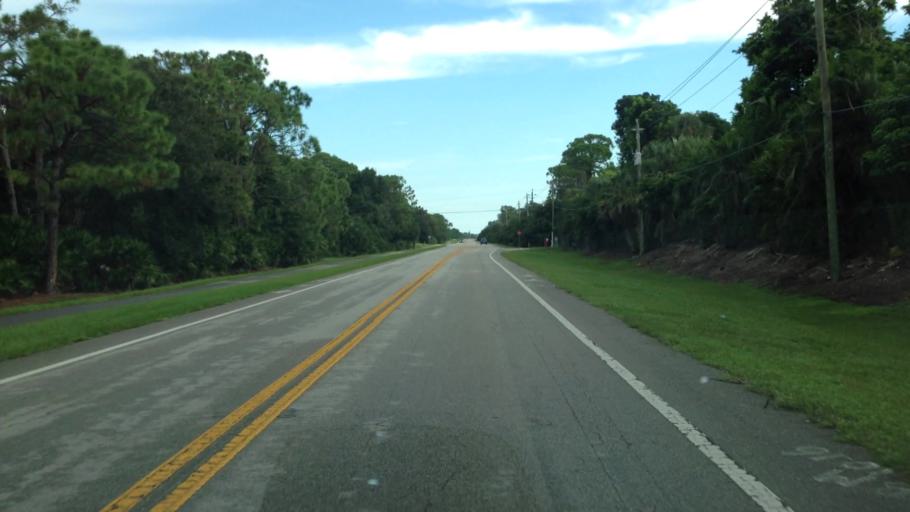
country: US
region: Florida
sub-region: Collier County
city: Naples Park
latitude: 26.3074
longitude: -81.8188
